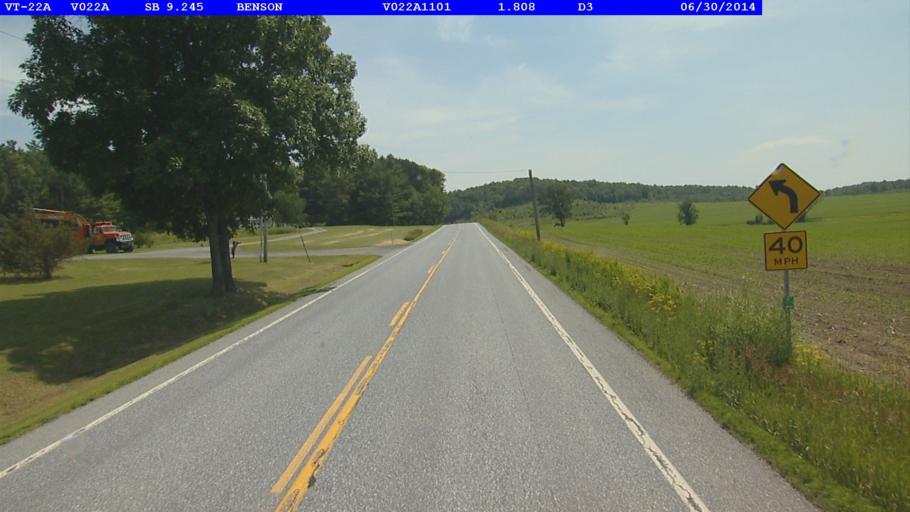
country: US
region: Vermont
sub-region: Rutland County
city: Fair Haven
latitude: 43.6947
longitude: -73.2936
